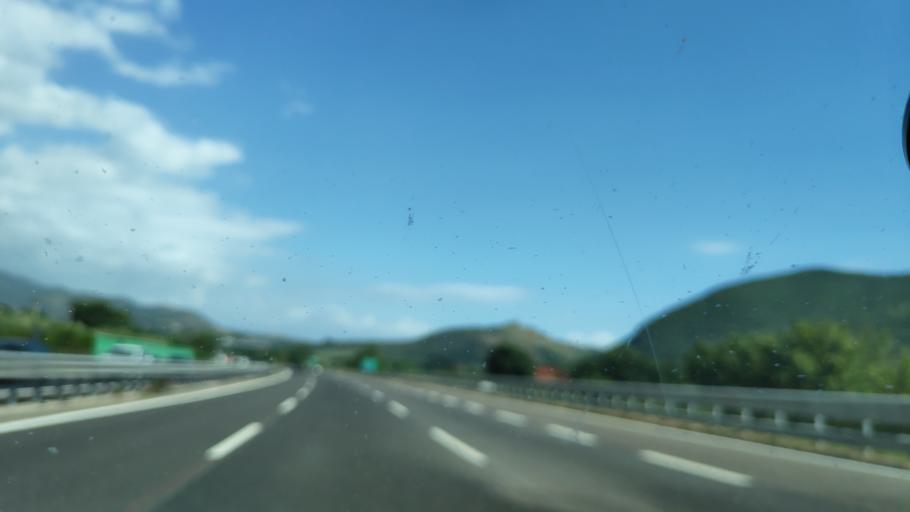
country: IT
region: Campania
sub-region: Provincia di Salerno
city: San Mango Piemonte
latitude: 40.6891
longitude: 14.8399
